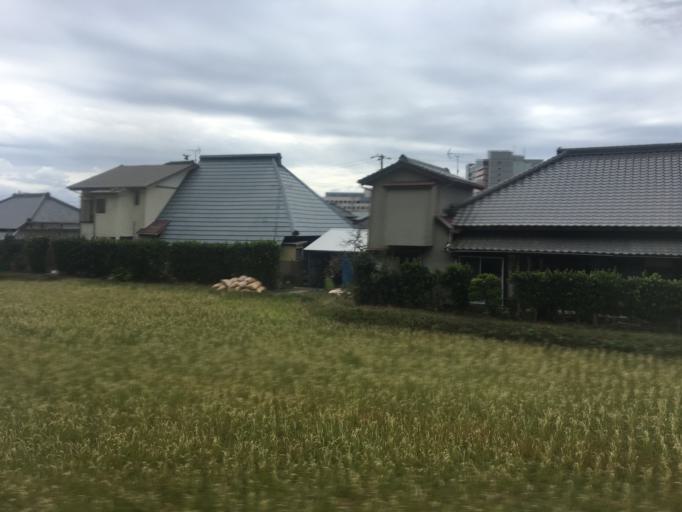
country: JP
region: Chiba
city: Kawaguchi
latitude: 35.1244
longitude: 140.1269
